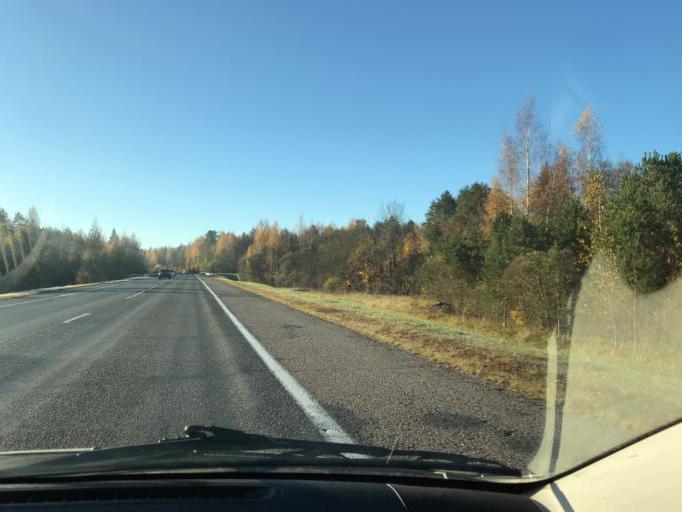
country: BY
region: Vitebsk
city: Vitebsk
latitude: 54.9022
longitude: 30.3766
